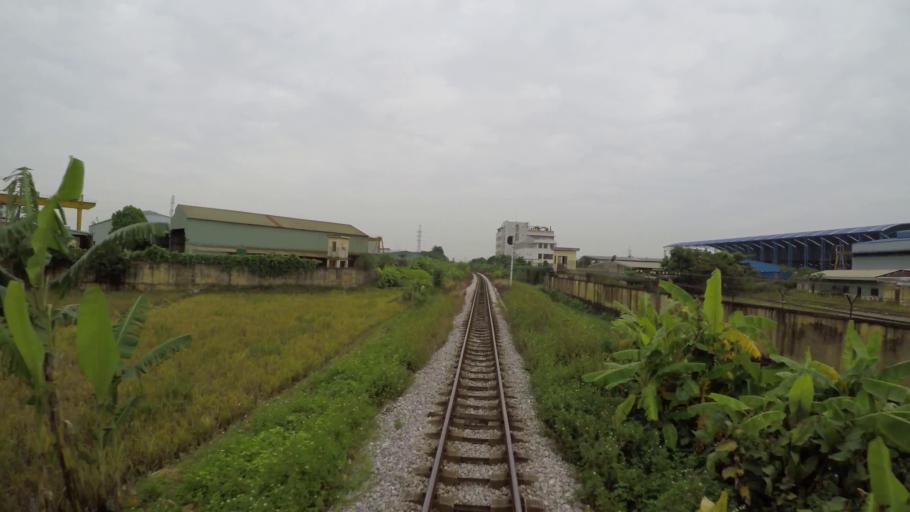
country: VN
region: Hai Phong
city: An Duong
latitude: 20.8993
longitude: 106.5800
